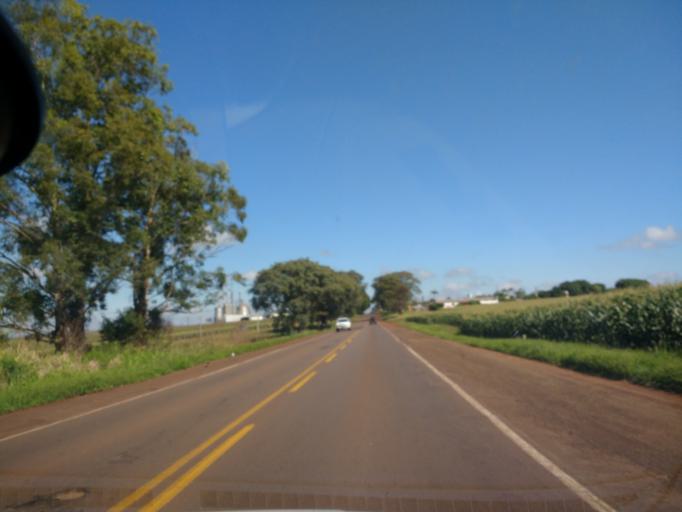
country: BR
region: Parana
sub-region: Terra Boa
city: Terra Boa
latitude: -23.6298
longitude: -52.4567
